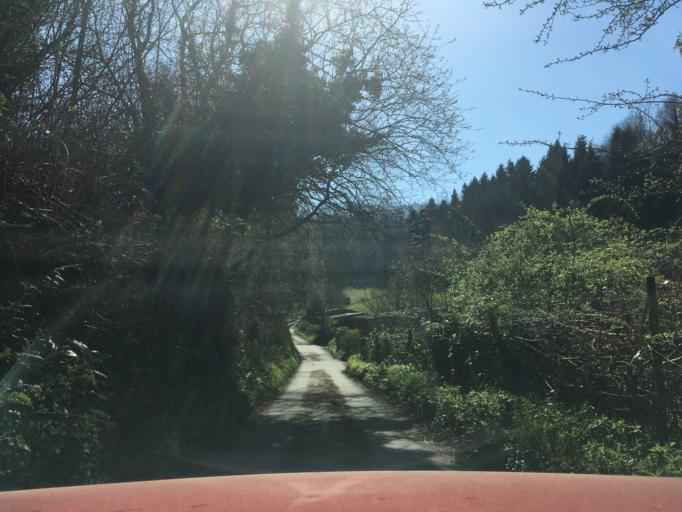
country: GB
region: England
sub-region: Gloucestershire
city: Wotton-under-Edge
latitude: 51.6529
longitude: -2.3457
